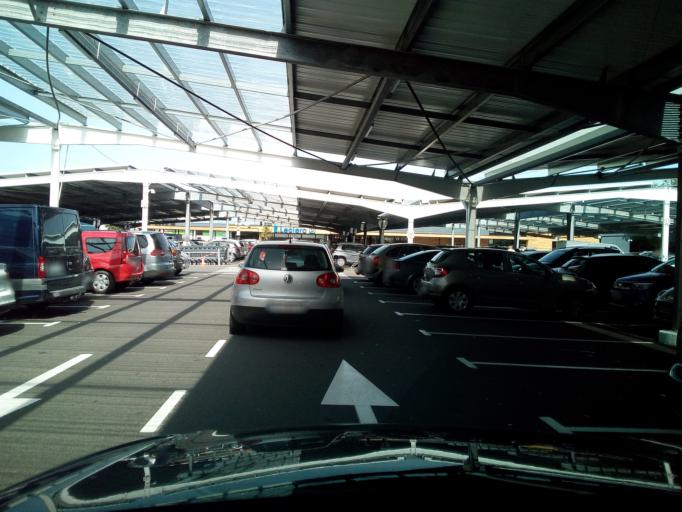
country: FR
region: Brittany
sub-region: Departement du Finistere
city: Landerneau
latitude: 48.4652
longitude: -4.2626
